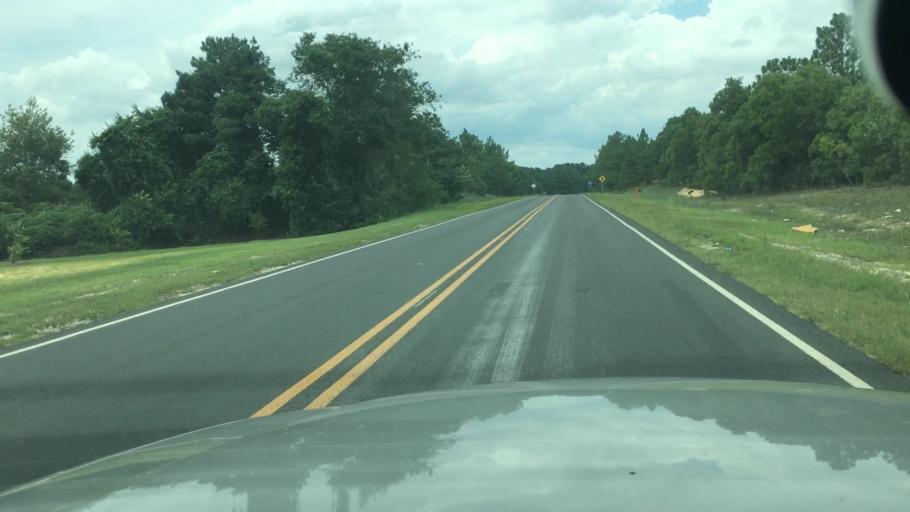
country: US
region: North Carolina
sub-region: Cumberland County
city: Hope Mills
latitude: 34.9719
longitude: -78.8933
